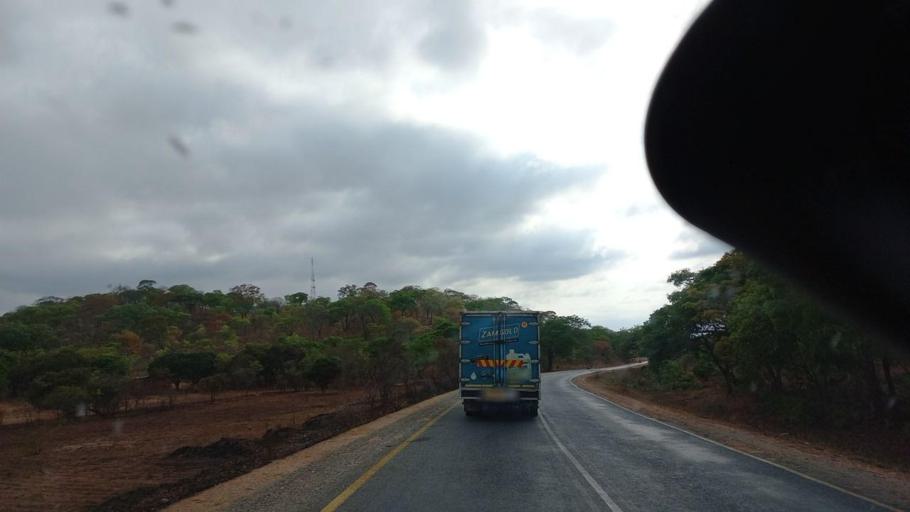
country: ZM
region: Lusaka
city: Chongwe
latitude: -15.2711
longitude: 28.8941
